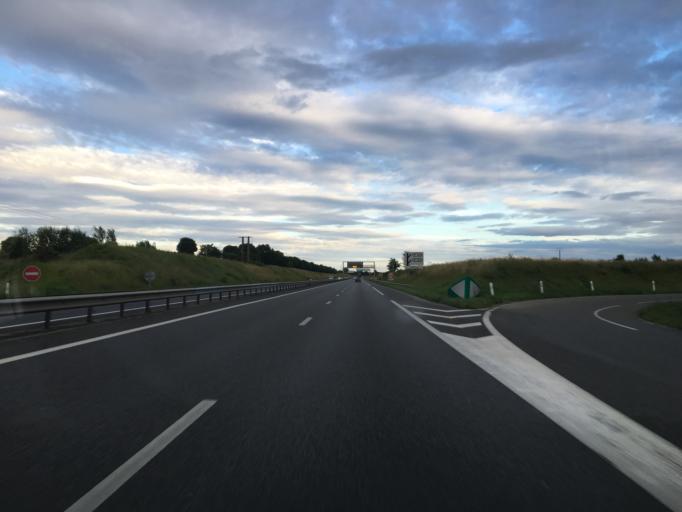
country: FR
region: Ile-de-France
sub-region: Departement de Seine-et-Marne
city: Moissy-Cramayel
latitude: 48.6460
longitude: 2.6228
